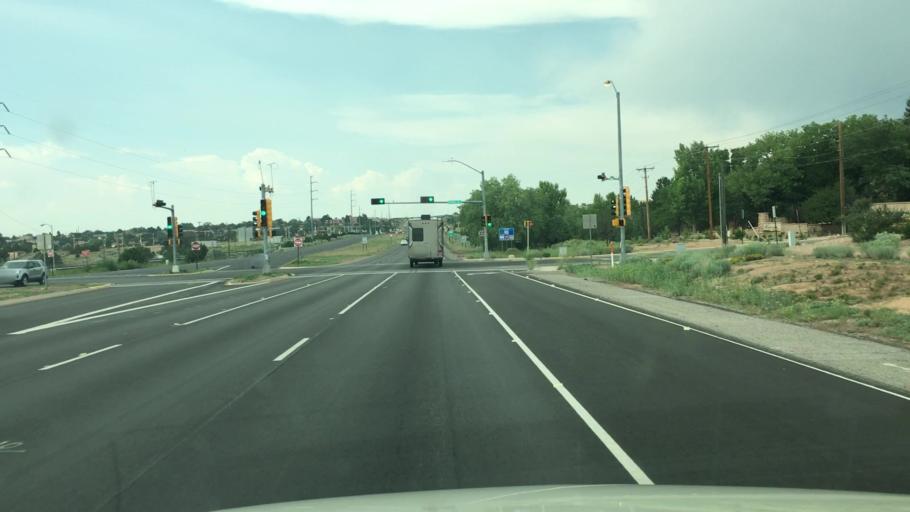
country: US
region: New Mexico
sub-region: Santa Fe County
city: Santa Fe
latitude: 35.6416
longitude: -105.9562
